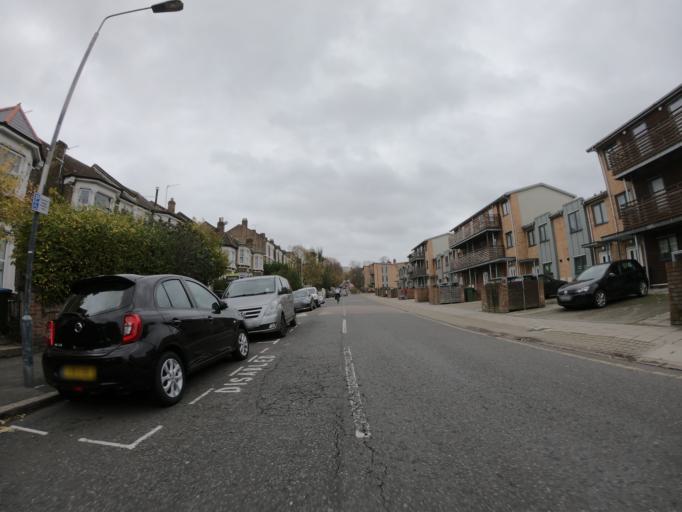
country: GB
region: England
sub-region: Greater London
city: Blackheath
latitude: 51.4833
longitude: 0.0292
